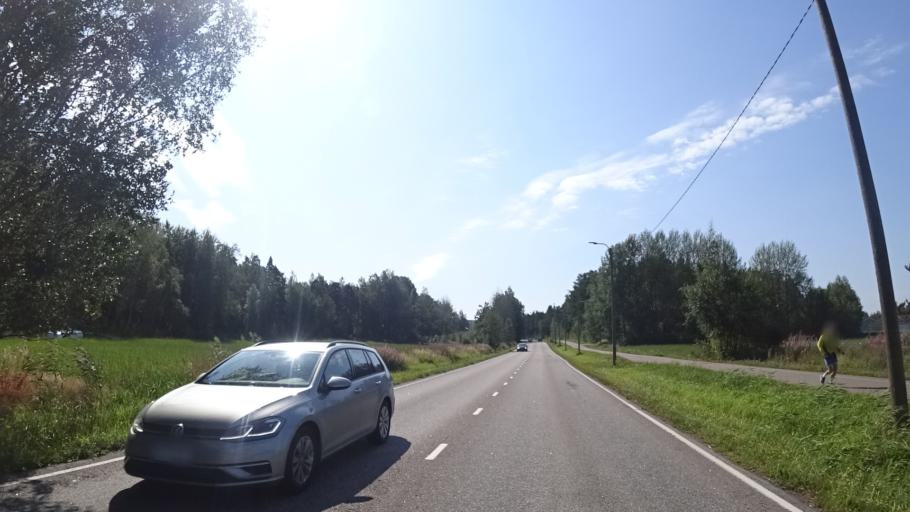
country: FI
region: Kymenlaakso
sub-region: Kotka-Hamina
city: Karhula
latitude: 60.5072
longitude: 26.9640
